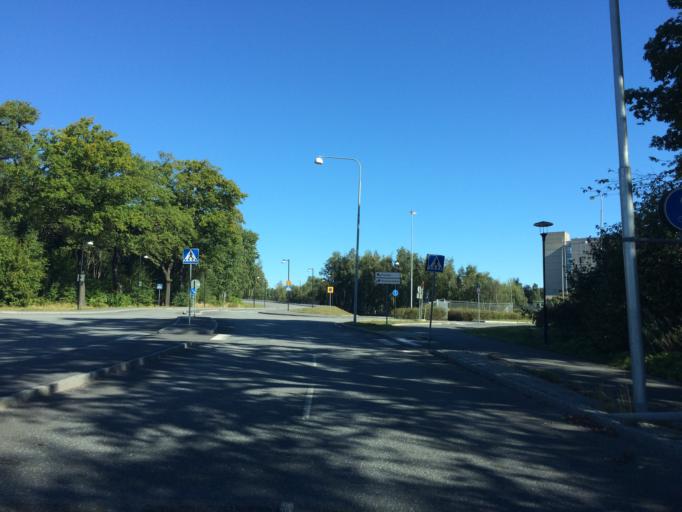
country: SE
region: Stockholm
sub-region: Solna Kommun
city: Solna
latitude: 59.3487
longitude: 18.0108
